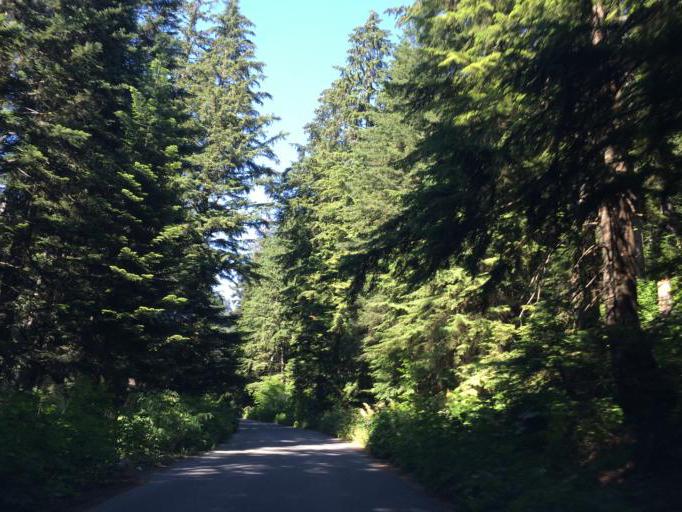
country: US
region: Washington
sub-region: King County
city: Tanner
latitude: 47.4178
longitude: -121.4362
